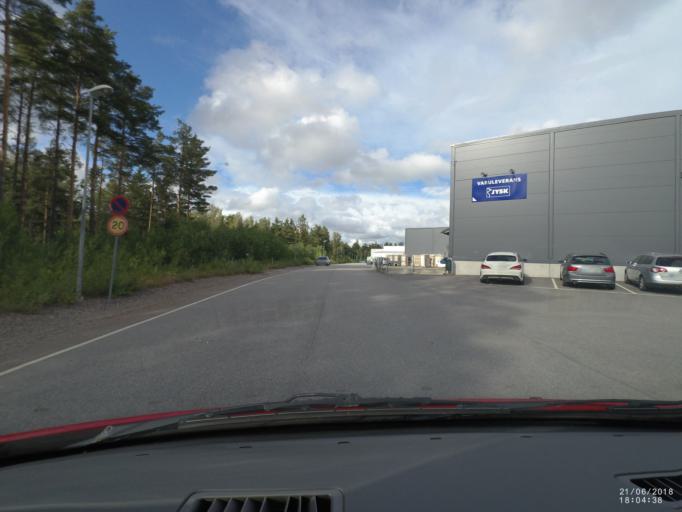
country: SE
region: Soedermanland
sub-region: Nykopings Kommun
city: Nykoping
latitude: 58.7714
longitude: 17.0126
